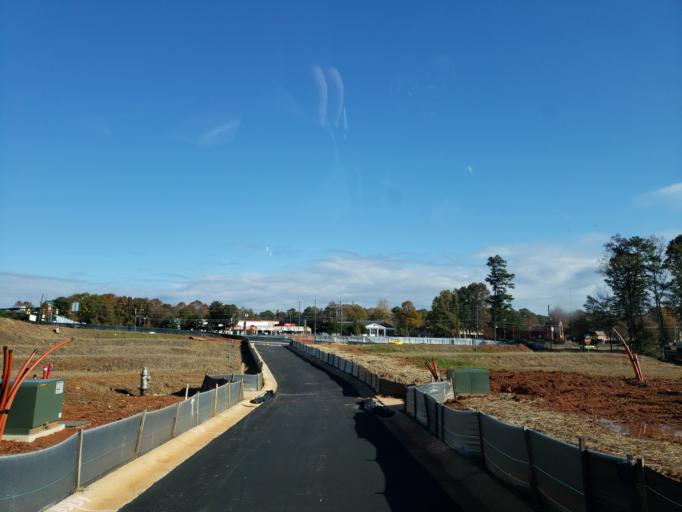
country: US
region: Georgia
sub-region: Fulton County
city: Roswell
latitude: 33.9970
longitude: -84.3525
